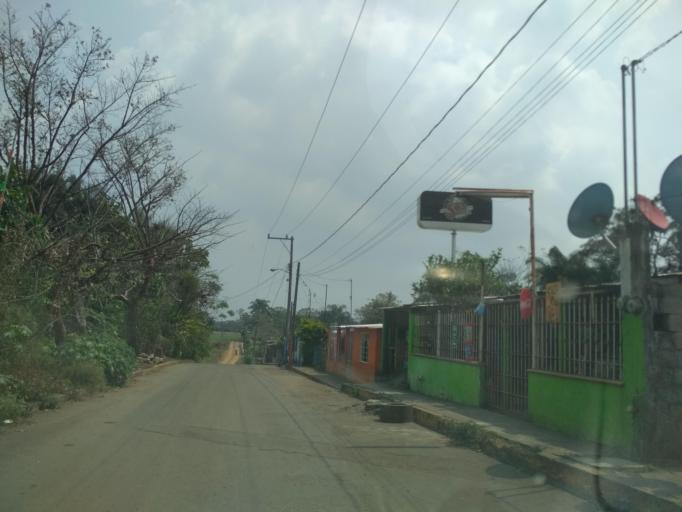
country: MX
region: Veracruz
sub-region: Cordoba
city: Fredepo
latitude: 18.8574
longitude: -96.9829
